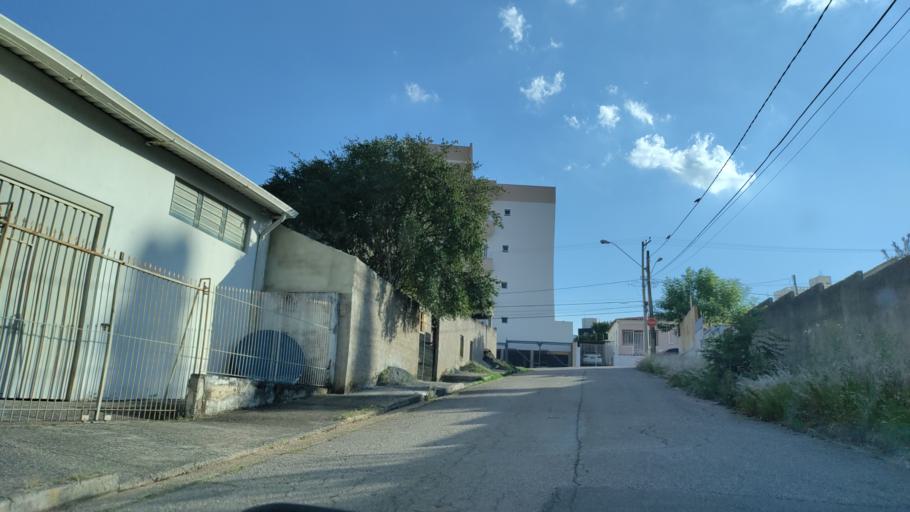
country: BR
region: Sao Paulo
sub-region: Sorocaba
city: Sorocaba
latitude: -23.4823
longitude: -47.4455
